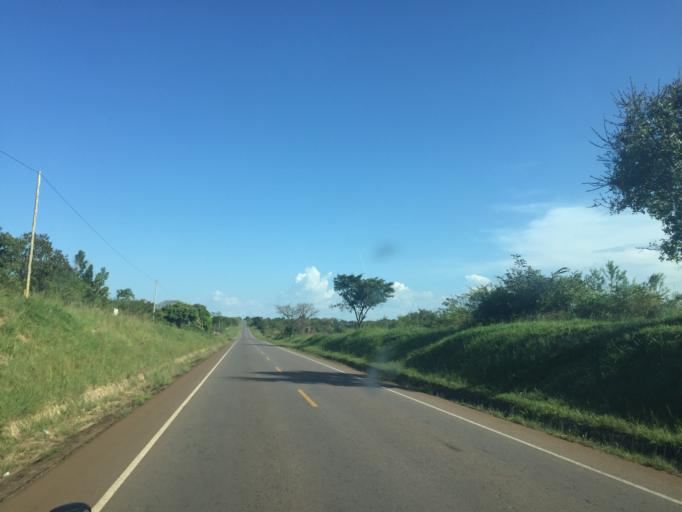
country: UG
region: Central Region
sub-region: Nakasongola District
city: Nakasongola
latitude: 1.3526
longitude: 32.3798
